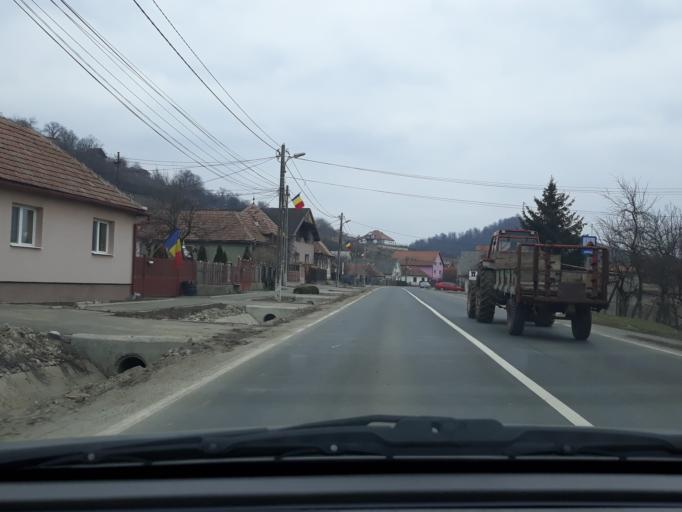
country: RO
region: Salaj
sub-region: Oras Simleu Silvaniei
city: Cehei
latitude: 47.2265
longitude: 22.7678
